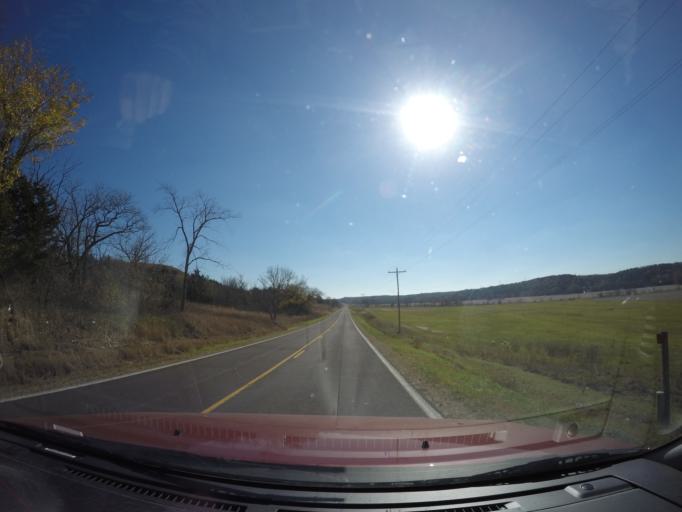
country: US
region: Kansas
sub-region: Geary County
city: Grandview Plaza
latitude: 38.9936
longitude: -96.7297
